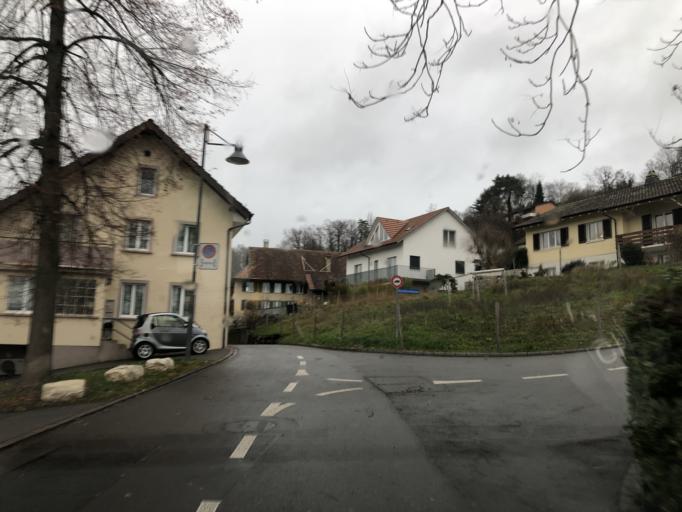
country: CH
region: Aargau
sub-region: Bezirk Baden
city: Untersiggenthal
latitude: 47.4994
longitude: 8.2651
